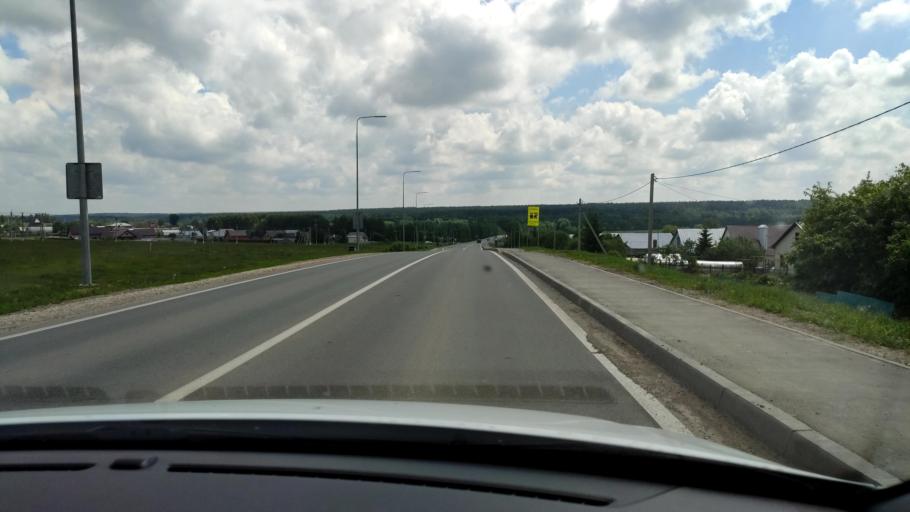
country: RU
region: Tatarstan
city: Vysokaya Gora
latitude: 55.9896
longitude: 49.3134
